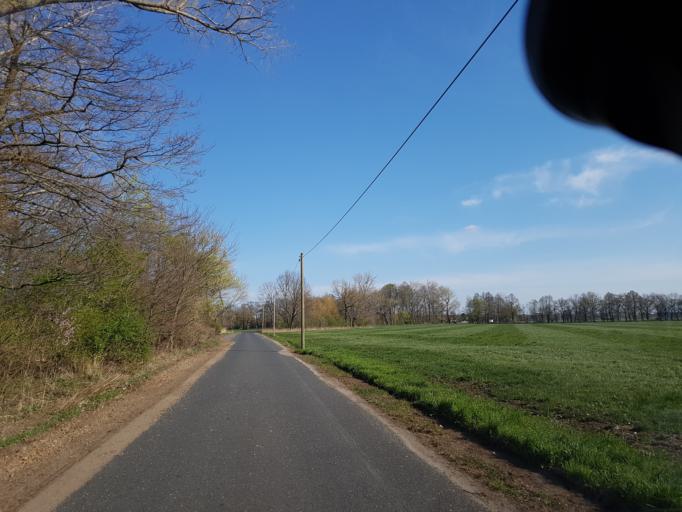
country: DE
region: Brandenburg
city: Falkenberg
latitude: 51.6340
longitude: 13.3077
